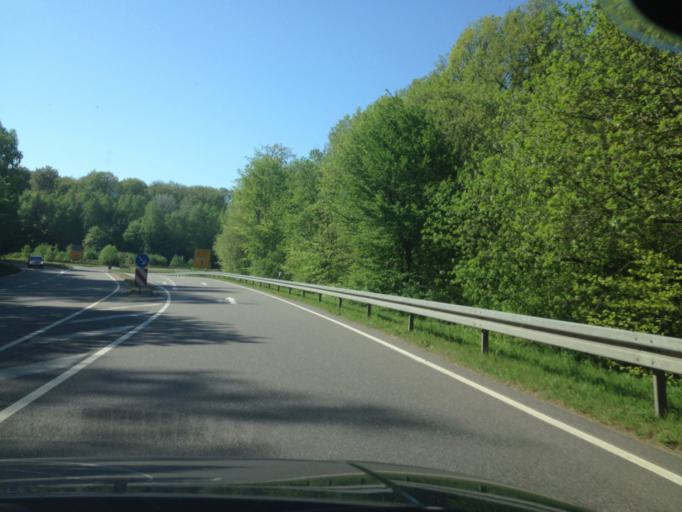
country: DE
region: Saarland
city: Sulzbach
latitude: 49.2745
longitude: 7.0643
